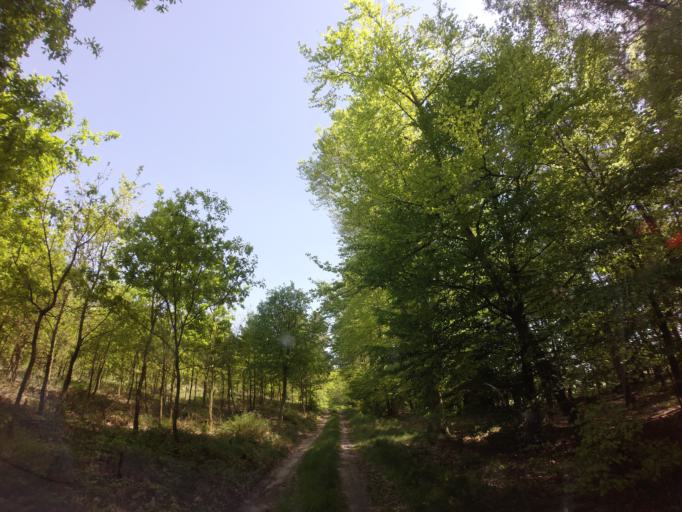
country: PL
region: West Pomeranian Voivodeship
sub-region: Powiat choszczenski
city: Pelczyce
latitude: 52.9566
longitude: 15.3152
